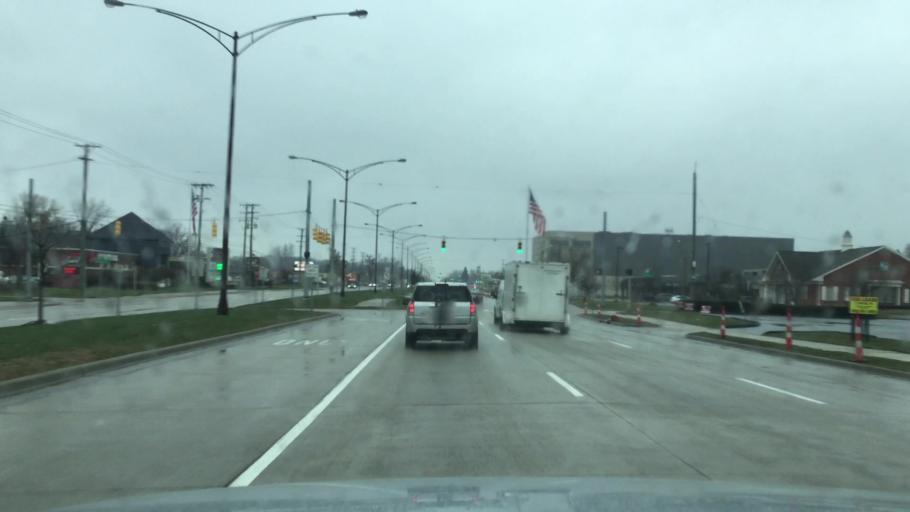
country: US
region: Michigan
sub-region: Oakland County
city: Troy
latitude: 42.5727
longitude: -83.1281
